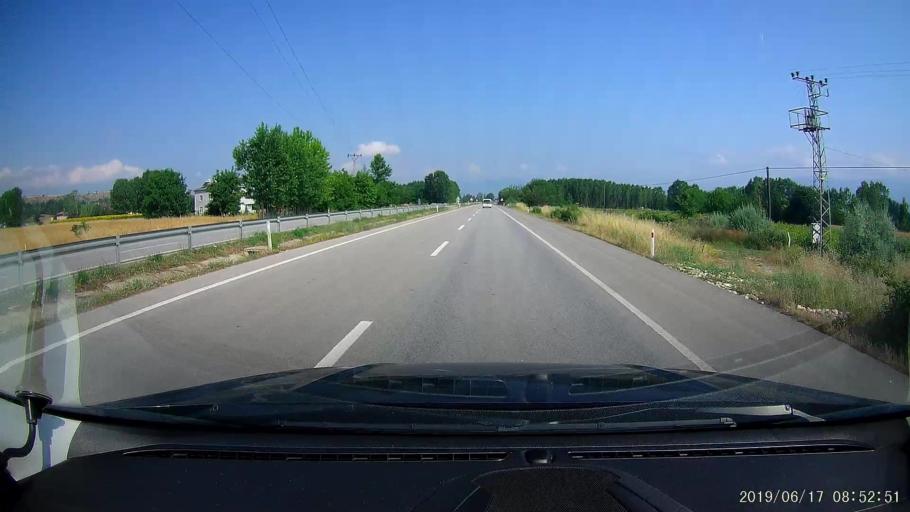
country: TR
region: Tokat
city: Erbaa
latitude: 40.7031
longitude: 36.4902
